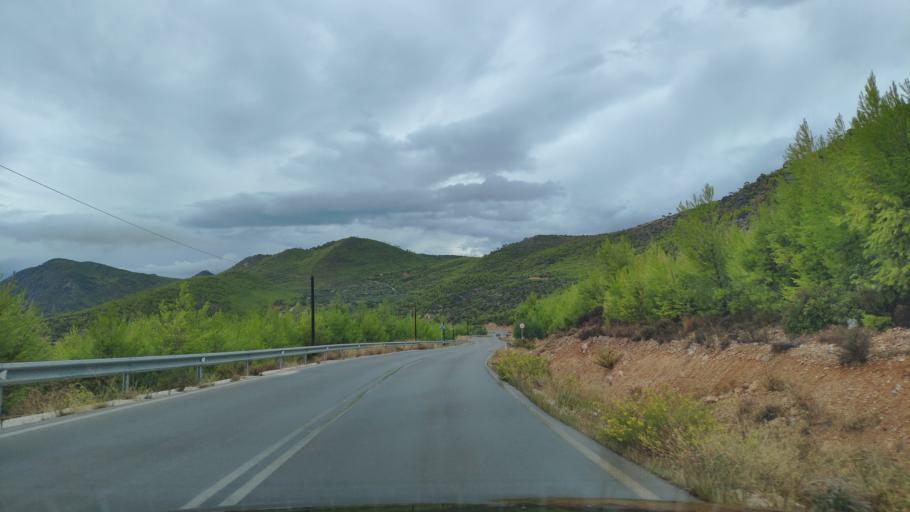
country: GR
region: Peloponnese
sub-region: Nomos Korinthias
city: Perachora
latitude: 38.0303
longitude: 22.9291
